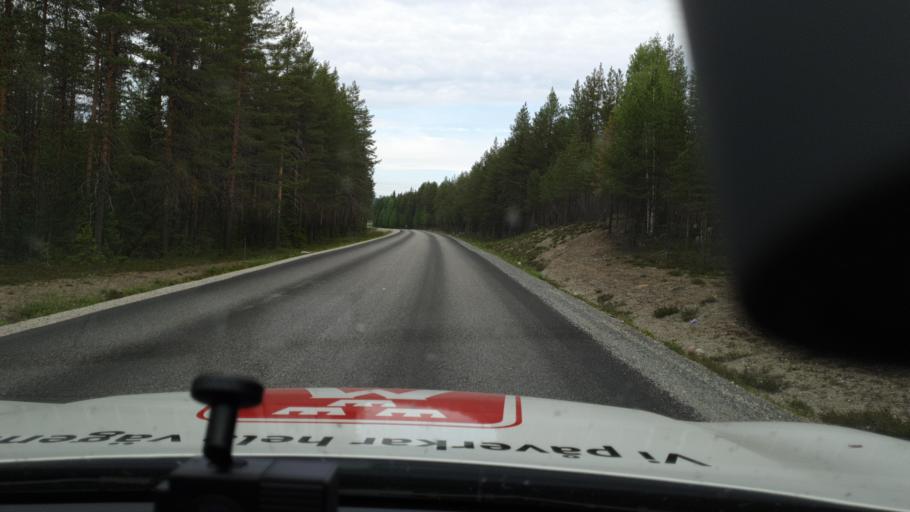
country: SE
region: Vaesterbotten
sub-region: Mala Kommun
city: Mala
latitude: 64.9472
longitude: 18.6147
